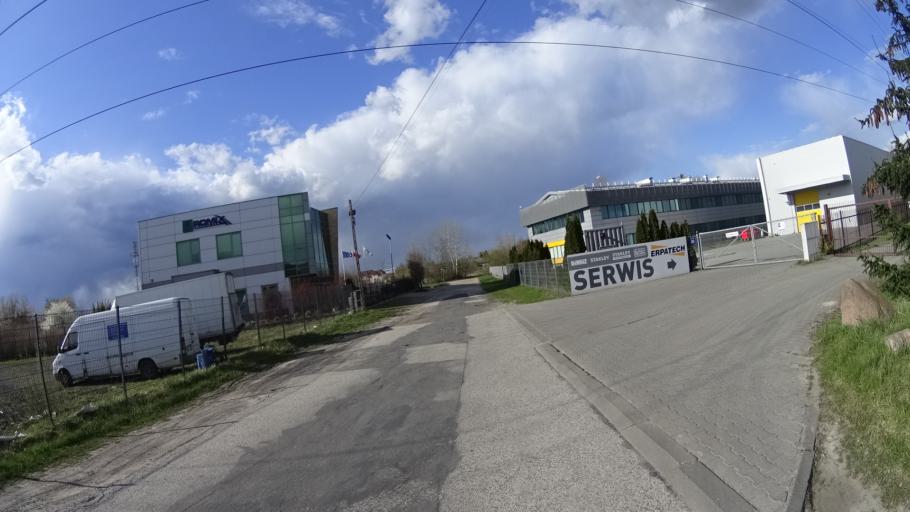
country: PL
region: Masovian Voivodeship
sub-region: Powiat warszawski zachodni
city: Babice
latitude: 52.2848
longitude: 20.8708
